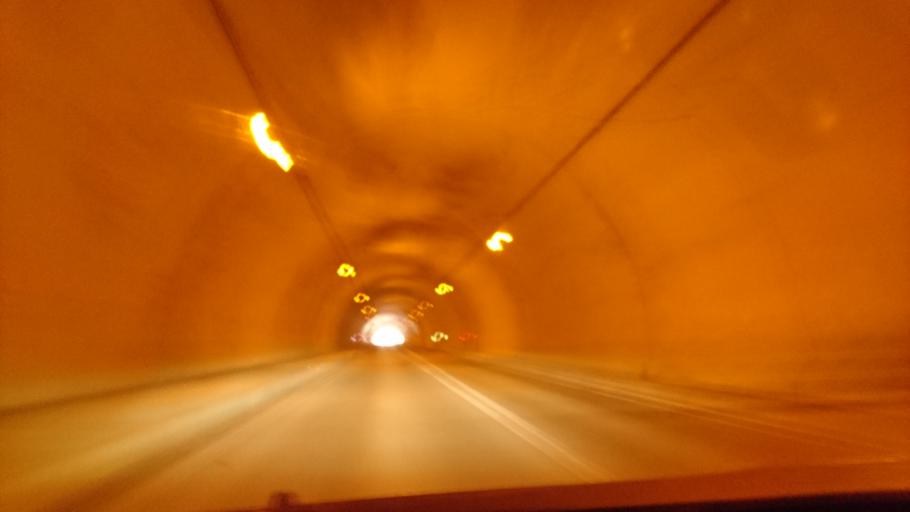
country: JP
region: Iwate
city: Ichinoseki
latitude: 38.9001
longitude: 140.9185
